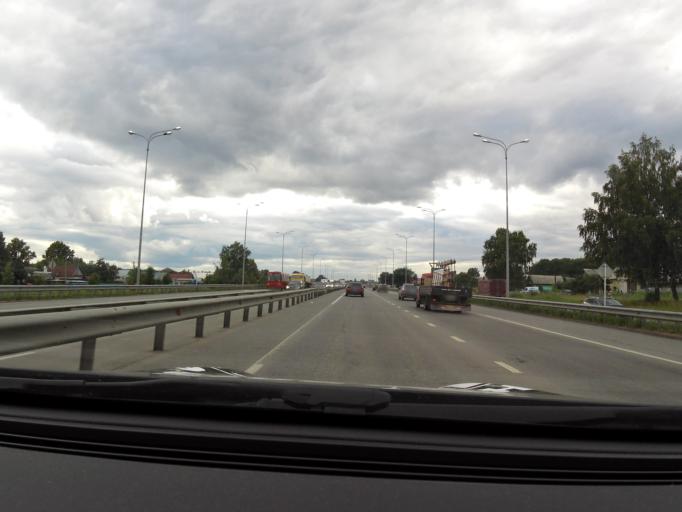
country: RU
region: Tatarstan
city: Osinovo
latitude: 55.8487
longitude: 48.9032
